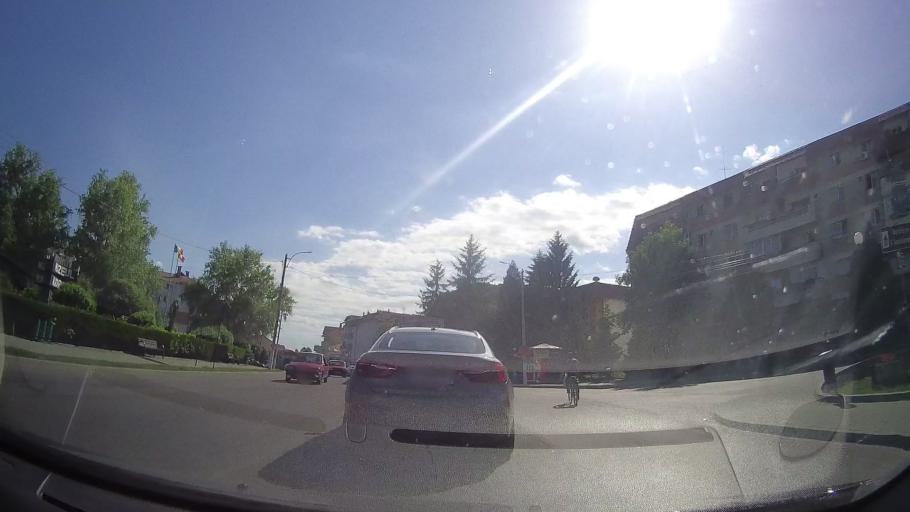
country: RO
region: Prahova
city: Valenii de Munte
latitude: 45.1862
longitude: 26.0395
